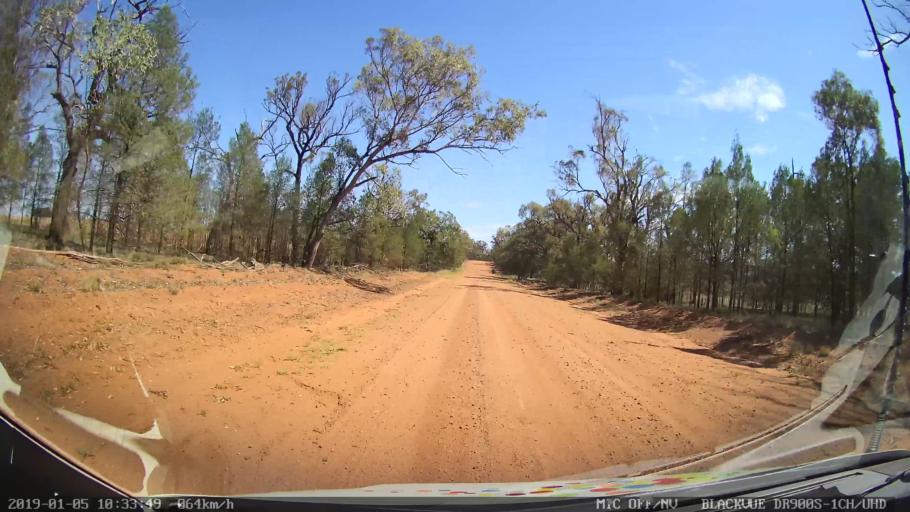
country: AU
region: New South Wales
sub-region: Gilgandra
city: Gilgandra
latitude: -31.5039
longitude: 148.9296
